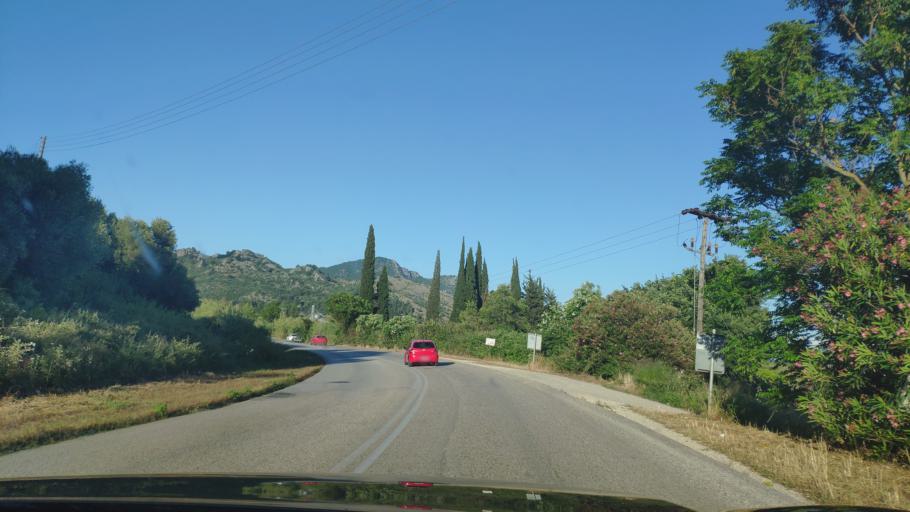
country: GR
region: Epirus
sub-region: Nomos Prevezis
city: Louros
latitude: 39.1760
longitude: 20.7714
